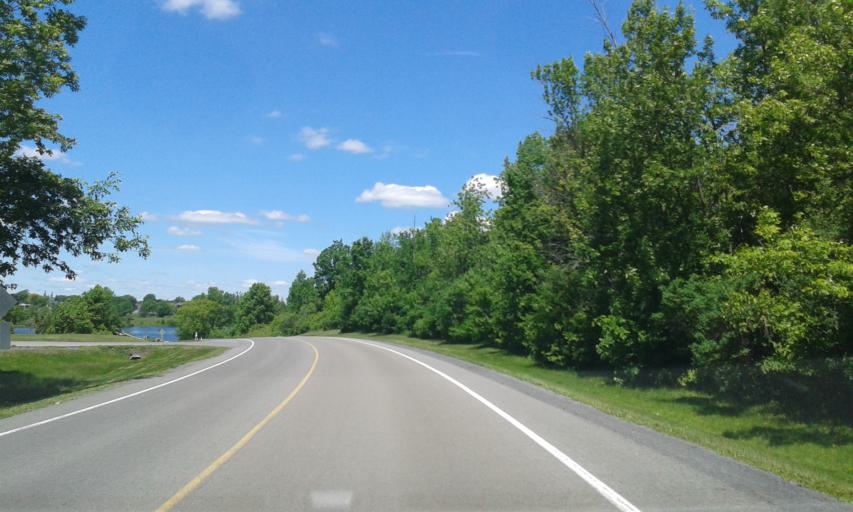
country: US
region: New York
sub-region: St. Lawrence County
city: Massena
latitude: 45.0187
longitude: -74.8929
